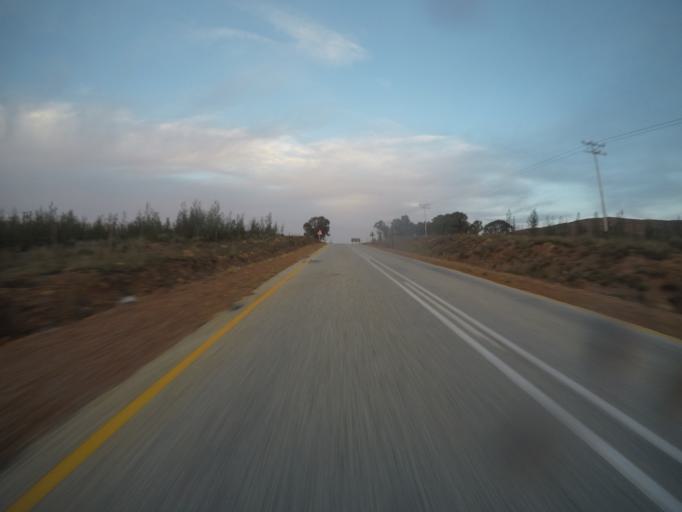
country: ZA
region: Western Cape
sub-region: Eden District Municipality
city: Plettenberg Bay
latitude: -33.7402
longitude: 23.4334
